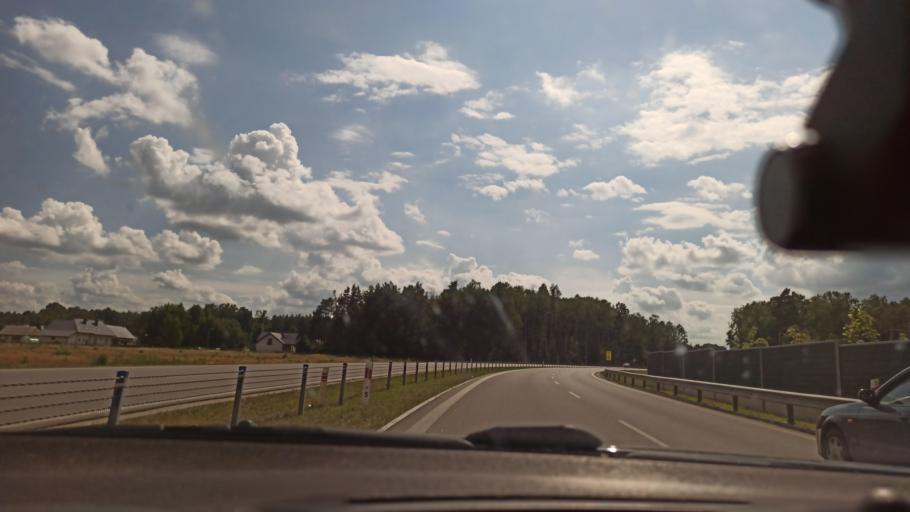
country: PL
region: Podlasie
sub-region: Powiat bialostocki
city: Turosn Koscielna
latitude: 53.0608
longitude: 23.0630
